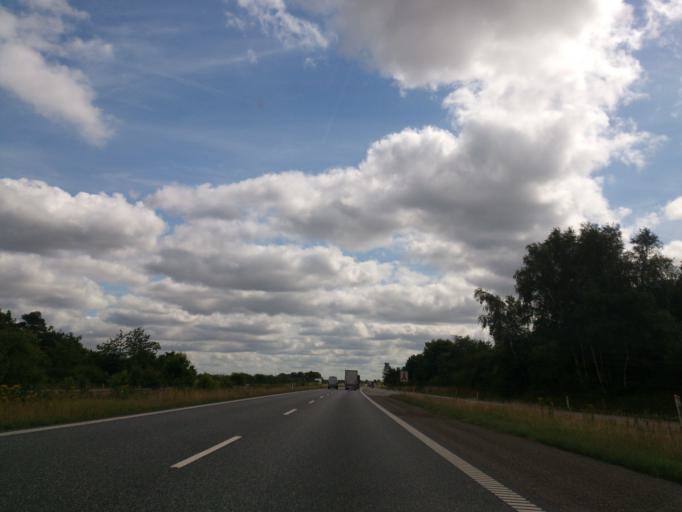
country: DK
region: South Denmark
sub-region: Aabenraa Kommune
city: Krusa
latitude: 54.9152
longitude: 9.3820
